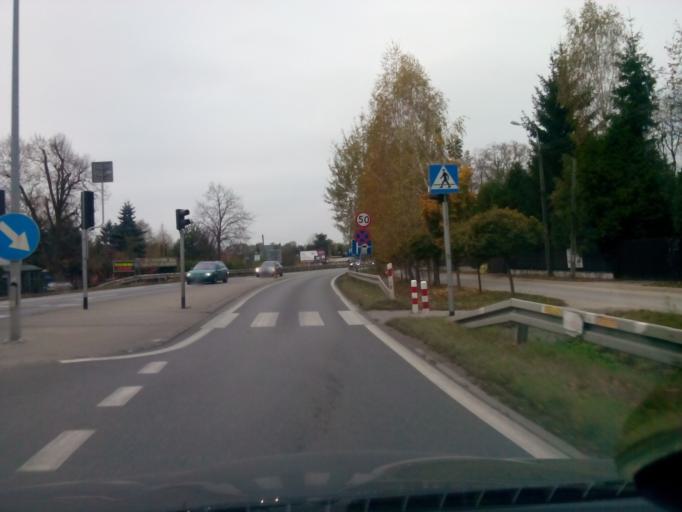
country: PL
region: Masovian Voivodeship
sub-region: Powiat pruszkowski
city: Otrebusy
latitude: 52.1309
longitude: 20.7564
